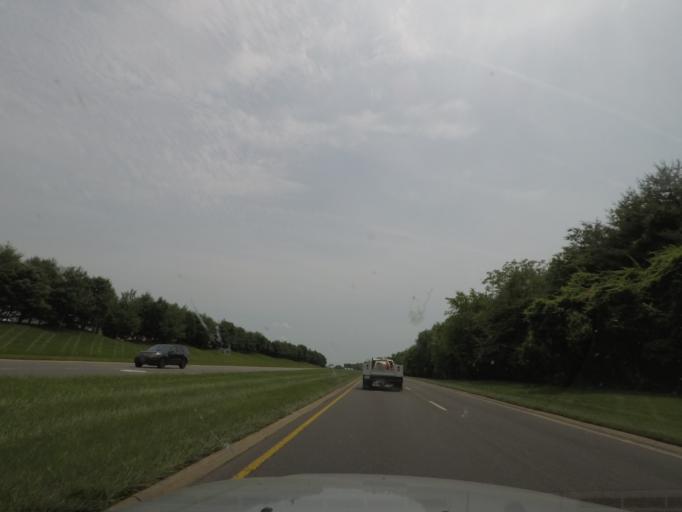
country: US
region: Virginia
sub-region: Prince William County
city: Haymarket
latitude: 38.8425
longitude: -77.6360
